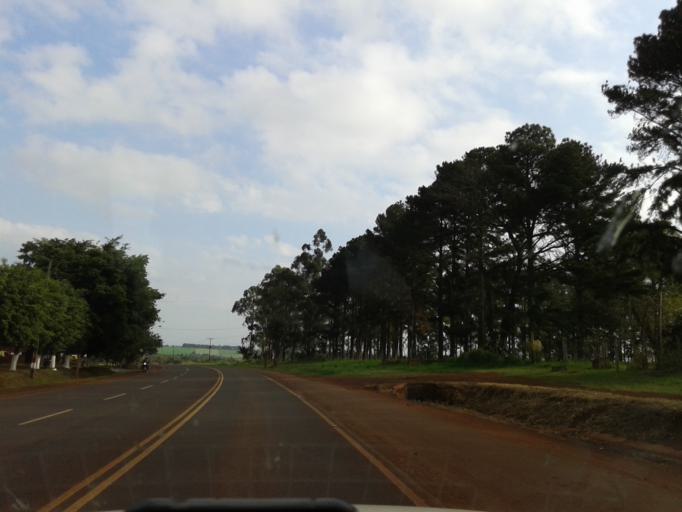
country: PY
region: Itapua
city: Edelira
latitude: -26.7244
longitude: -55.3469
